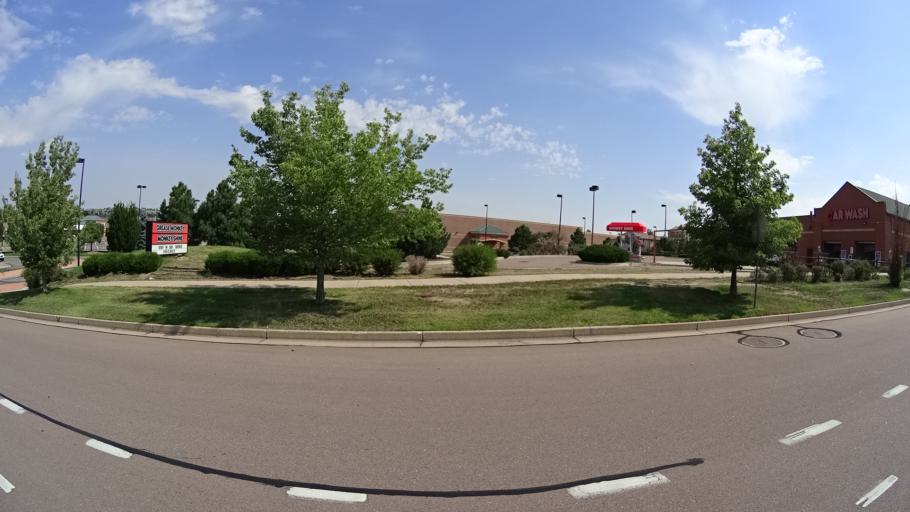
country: US
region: Colorado
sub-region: El Paso County
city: Cimarron Hills
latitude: 38.9313
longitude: -104.7393
